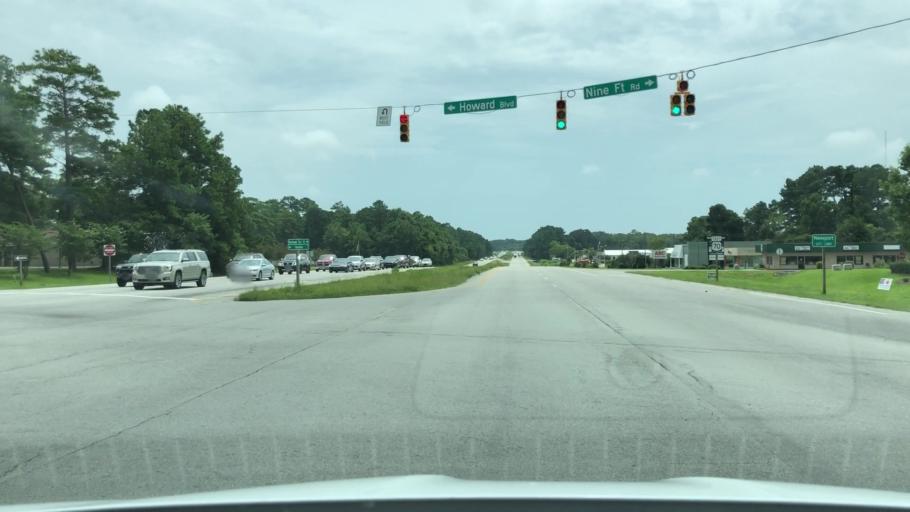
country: US
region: North Carolina
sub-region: Carteret County
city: Newport
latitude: 34.7893
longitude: -76.8764
